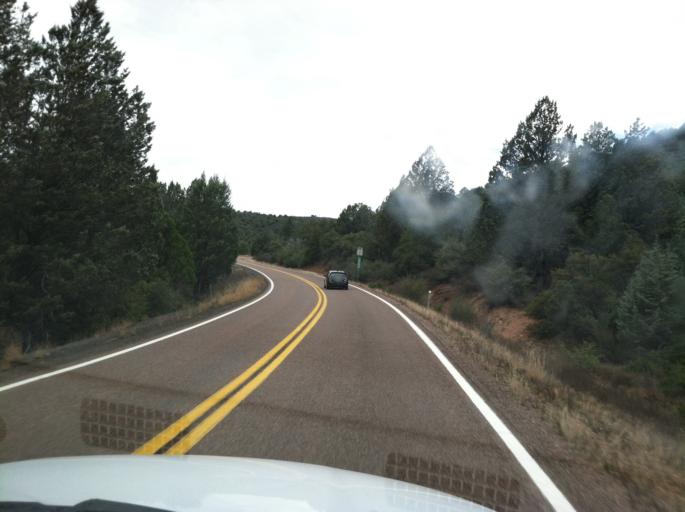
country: US
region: Arizona
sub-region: Gila County
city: Pine
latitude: 34.3181
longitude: -111.3819
